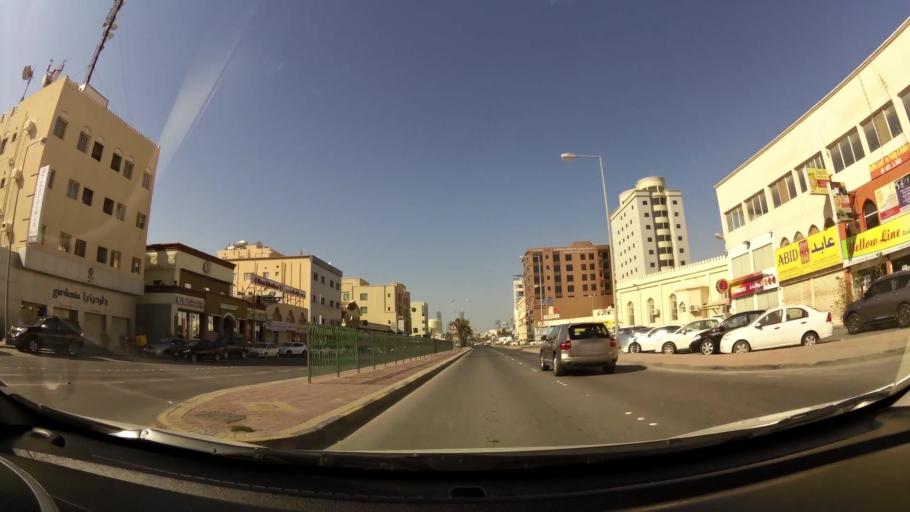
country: BH
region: Manama
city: Manama
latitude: 26.2099
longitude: 50.5756
